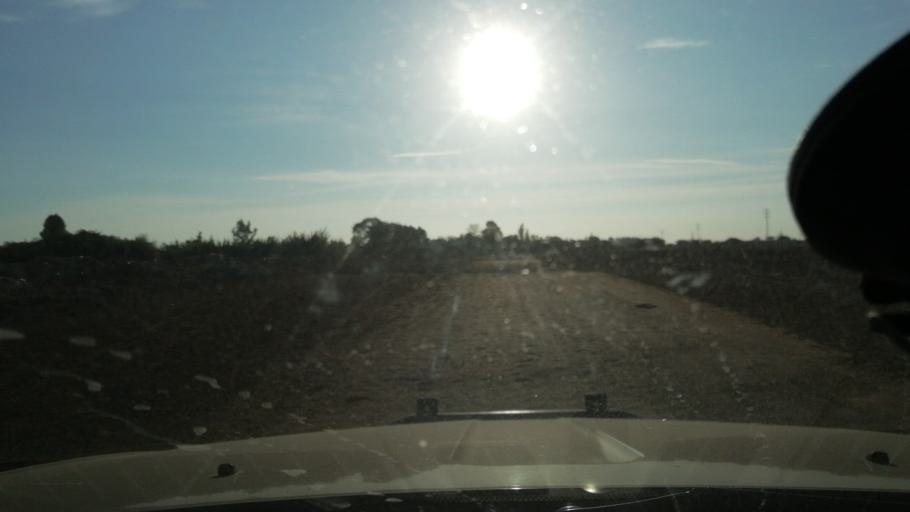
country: PE
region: Ica
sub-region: Provincia de Chincha
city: San Pedro
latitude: -13.3392
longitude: -76.1622
